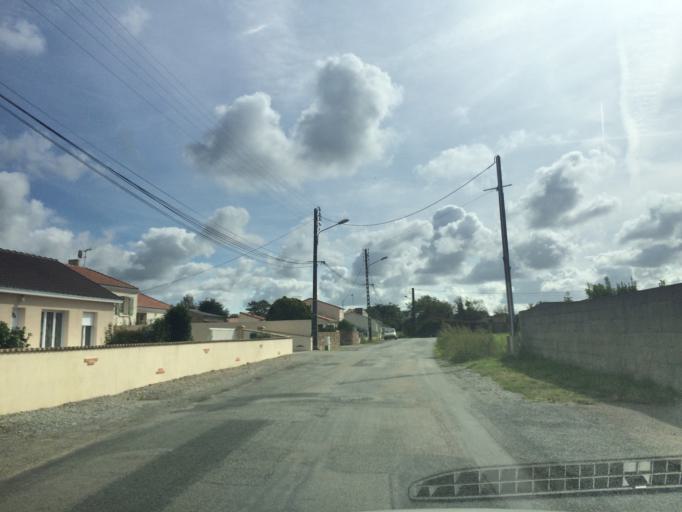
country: FR
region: Pays de la Loire
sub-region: Departement de la Loire-Atlantique
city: Chemere
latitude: 47.1167
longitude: -1.9272
